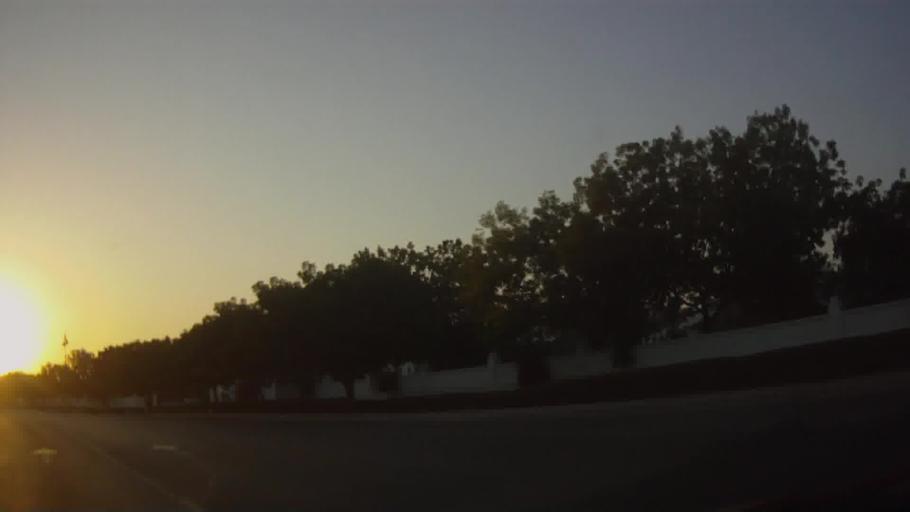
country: OM
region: Muhafazat Masqat
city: Bawshar
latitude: 23.6155
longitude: 58.4700
